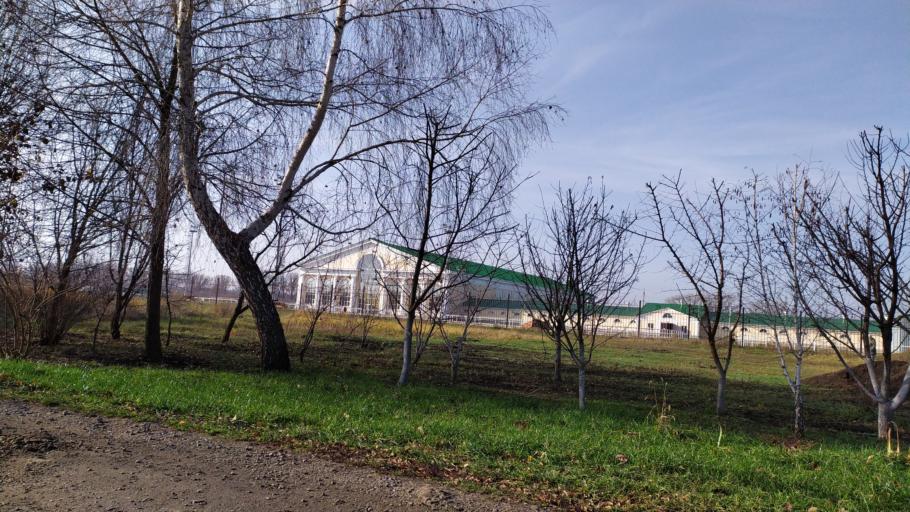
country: RU
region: Kursk
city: Kursk
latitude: 51.6421
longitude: 36.1314
